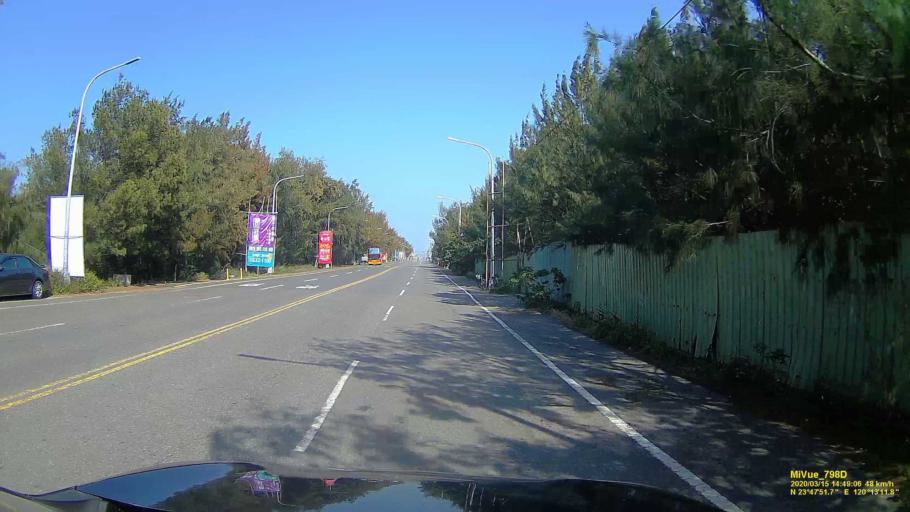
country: TW
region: Taiwan
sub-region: Yunlin
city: Douliu
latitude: 23.7977
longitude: 120.2200
